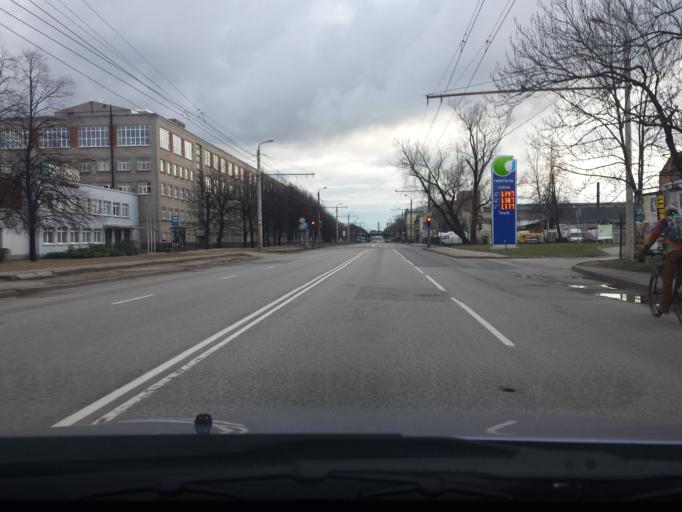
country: LV
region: Riga
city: Riga
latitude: 56.9802
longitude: 24.1163
